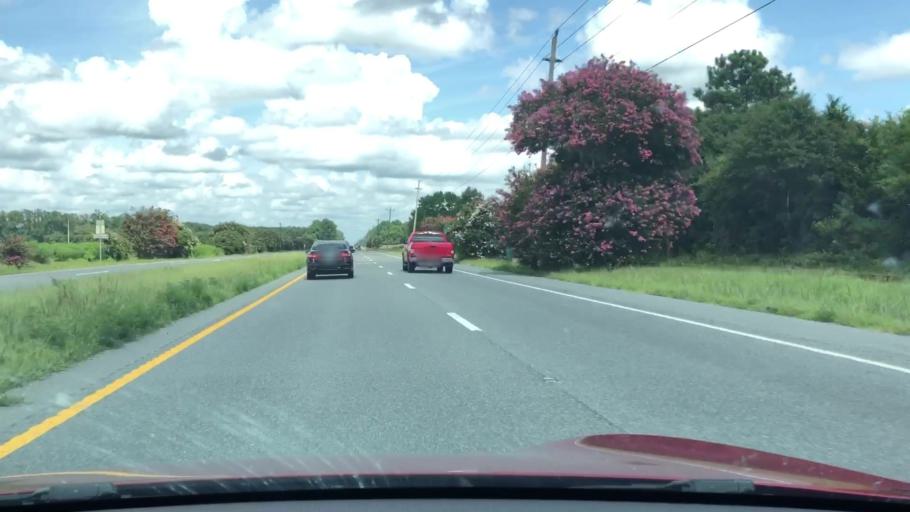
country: US
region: Virginia
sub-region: Northampton County
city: Exmore
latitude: 37.4589
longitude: -75.8691
